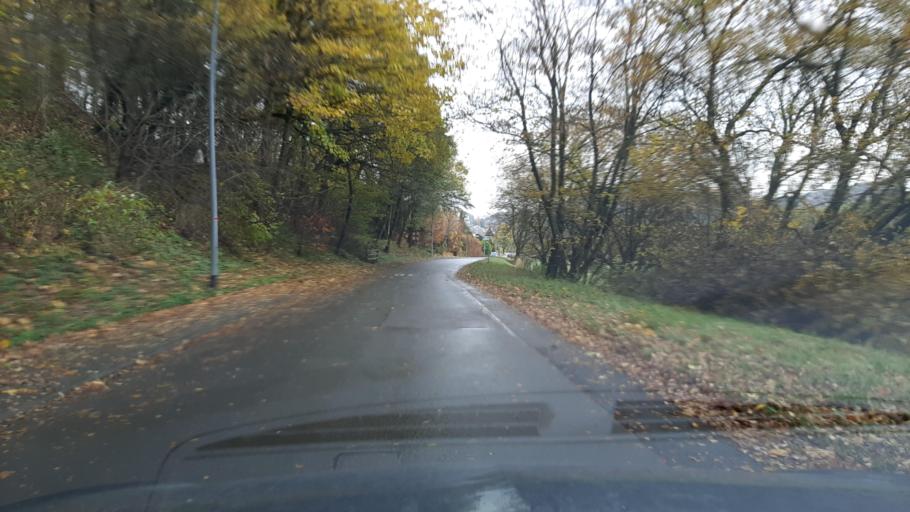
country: DE
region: Hesse
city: Willingen
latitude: 51.2883
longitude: 8.5867
